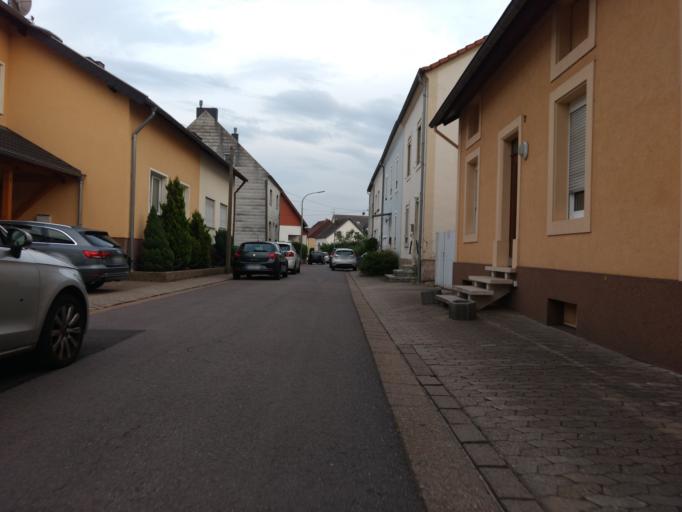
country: DE
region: Saarland
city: Wallerfangen
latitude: 49.3271
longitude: 6.7128
